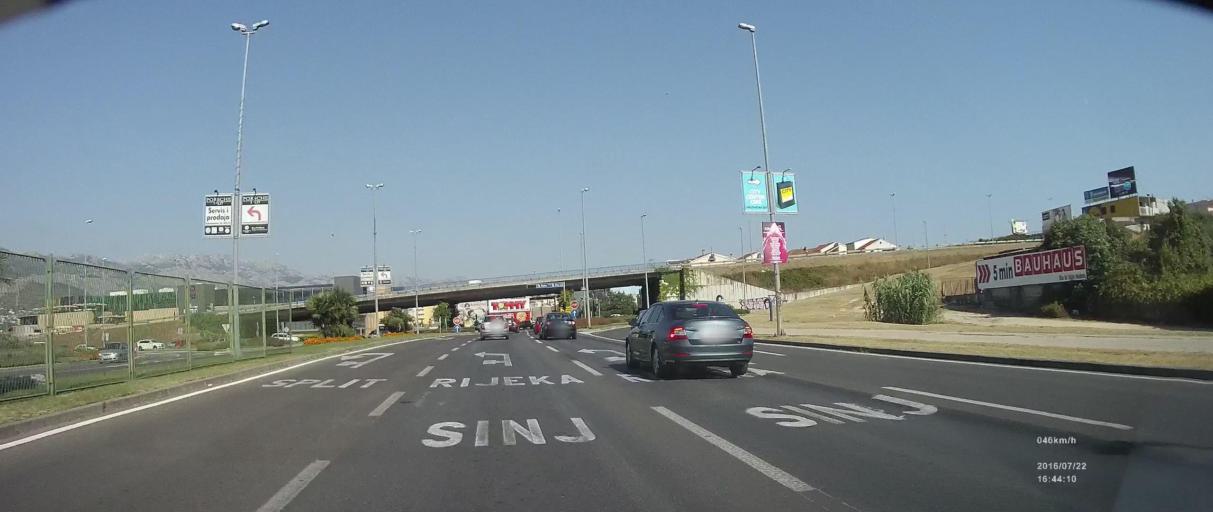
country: HR
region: Splitsko-Dalmatinska
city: Vranjic
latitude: 43.5186
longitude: 16.4794
